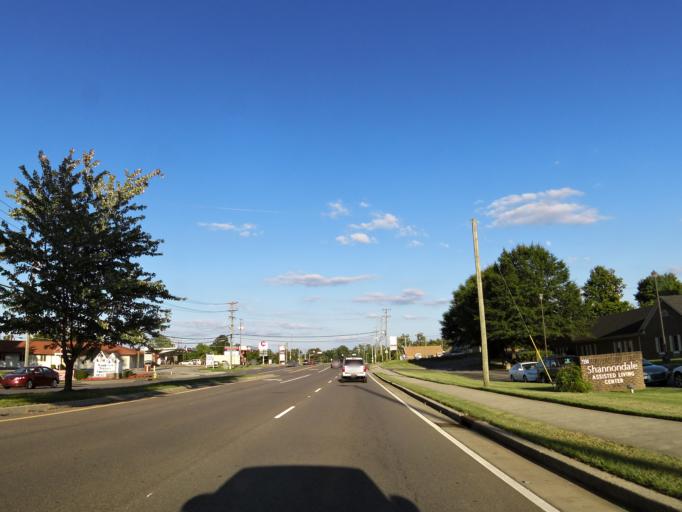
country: US
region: Tennessee
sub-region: Blount County
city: Louisville
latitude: 35.9412
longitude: -84.0402
